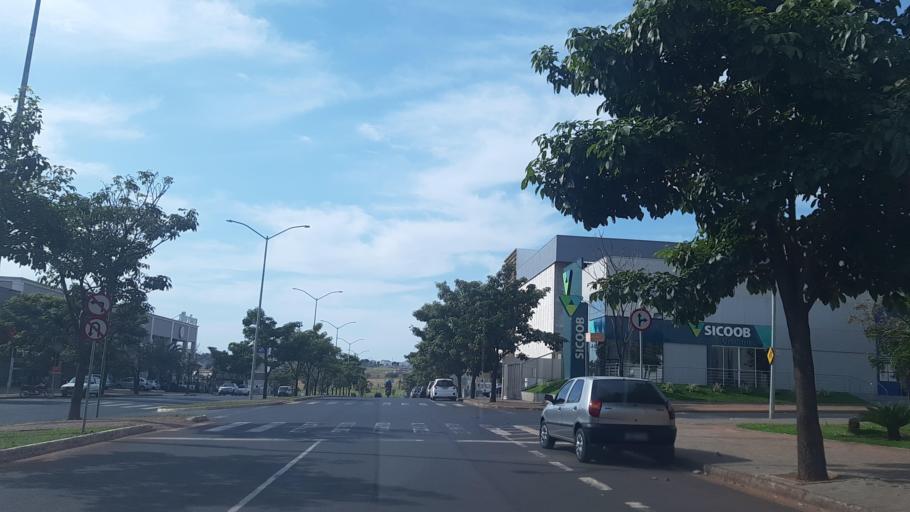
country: BR
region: Minas Gerais
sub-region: Uberlandia
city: Uberlandia
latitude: -18.8793
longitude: -48.2471
